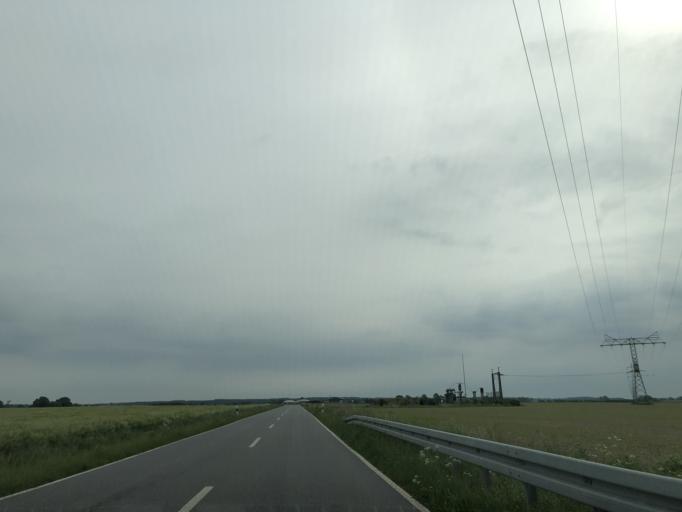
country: DE
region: Brandenburg
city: Gumtow
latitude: 52.9589
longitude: 12.1607
